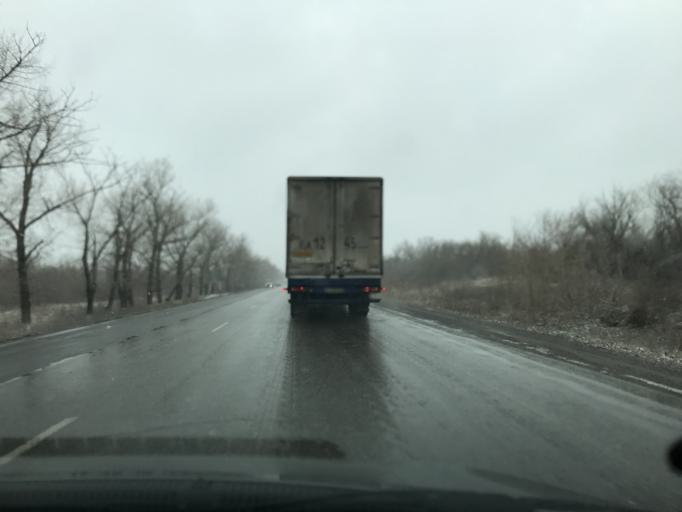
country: RU
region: Rostov
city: Bataysk
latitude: 47.0765
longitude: 39.7837
